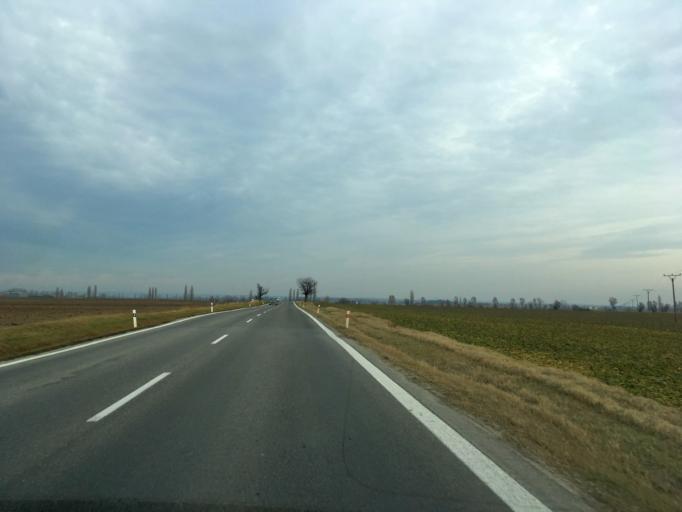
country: SK
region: Nitriansky
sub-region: Okres Nove Zamky
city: Nove Zamky
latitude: 47.9898
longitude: 18.2172
